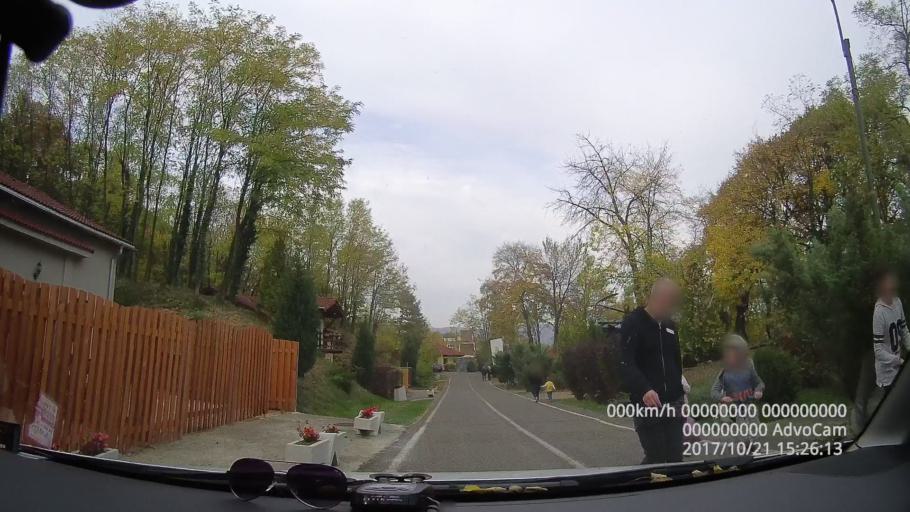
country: RO
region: Hunedoara
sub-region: Municipiul Deva
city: Deva
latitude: 45.8670
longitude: 22.9225
